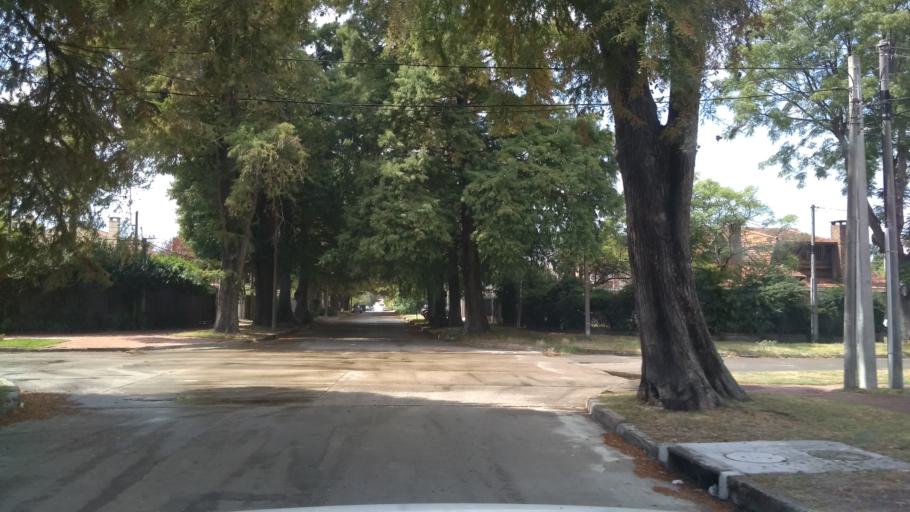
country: UY
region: Canelones
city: Paso de Carrasco
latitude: -34.8946
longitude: -56.0702
